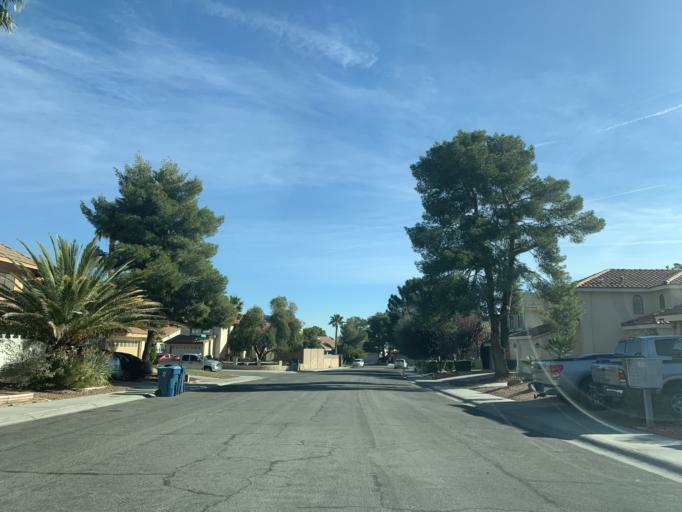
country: US
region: Nevada
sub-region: Clark County
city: Summerlin South
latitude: 36.1358
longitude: -115.2922
